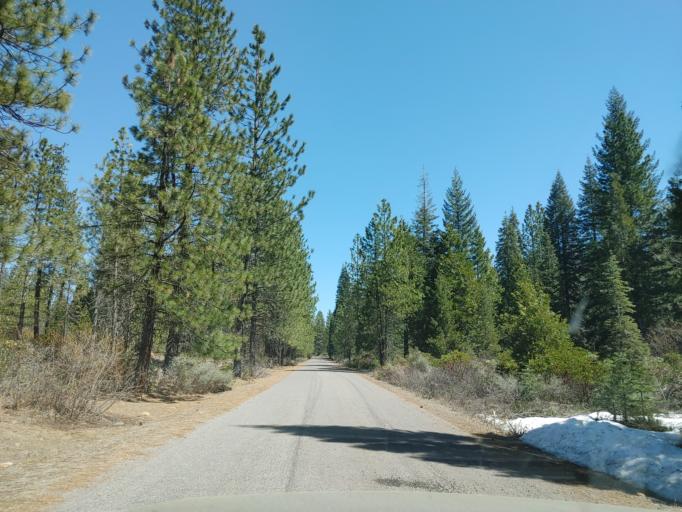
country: US
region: California
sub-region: Siskiyou County
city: McCloud
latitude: 41.2493
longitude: -121.9526
